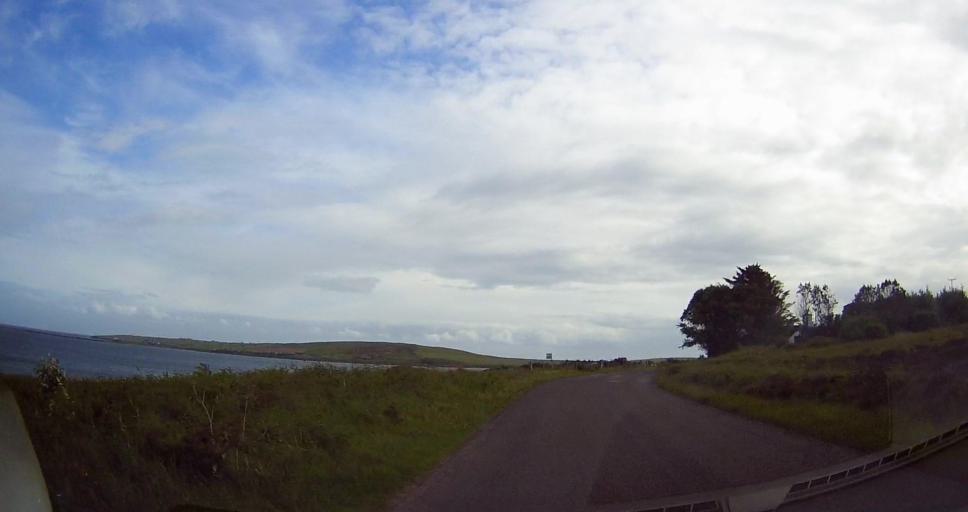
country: GB
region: Scotland
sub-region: Orkney Islands
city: Stromness
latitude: 58.7975
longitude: -3.2521
